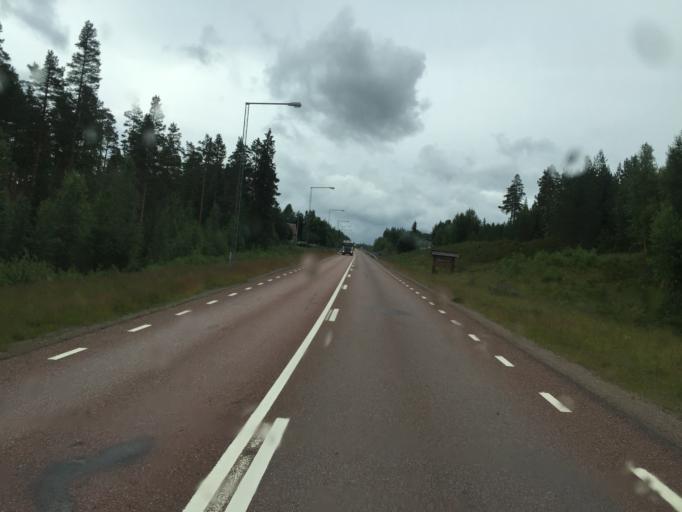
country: SE
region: Dalarna
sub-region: Malung-Saelens kommun
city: Malung
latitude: 60.6744
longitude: 13.6988
